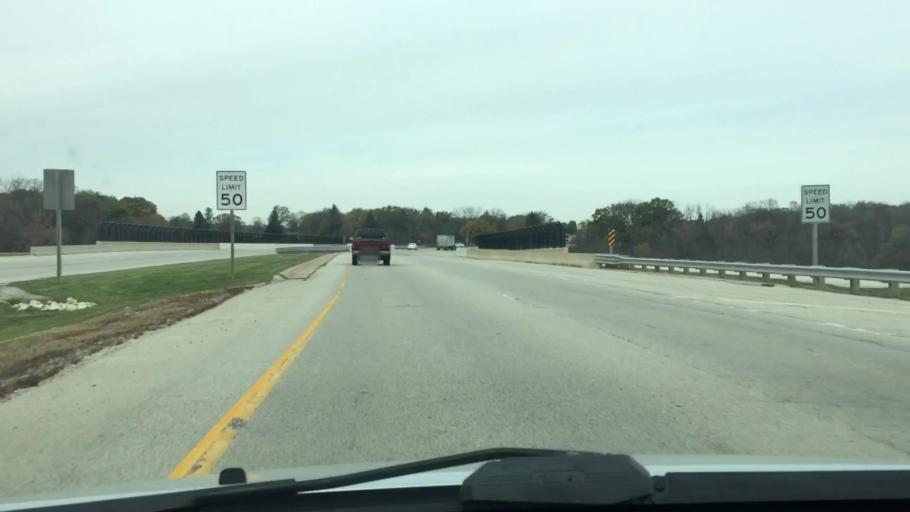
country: US
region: Wisconsin
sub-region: Milwaukee County
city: Franklin
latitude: 42.9131
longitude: -88.0434
